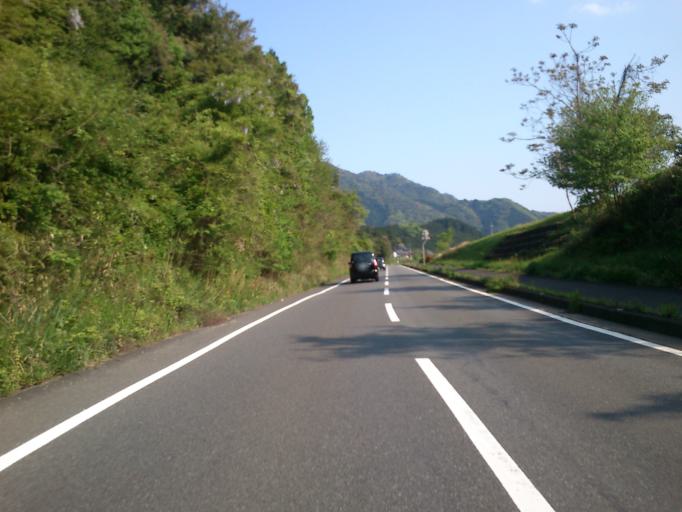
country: JP
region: Kyoto
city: Fukuchiyama
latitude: 35.2880
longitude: 135.0701
